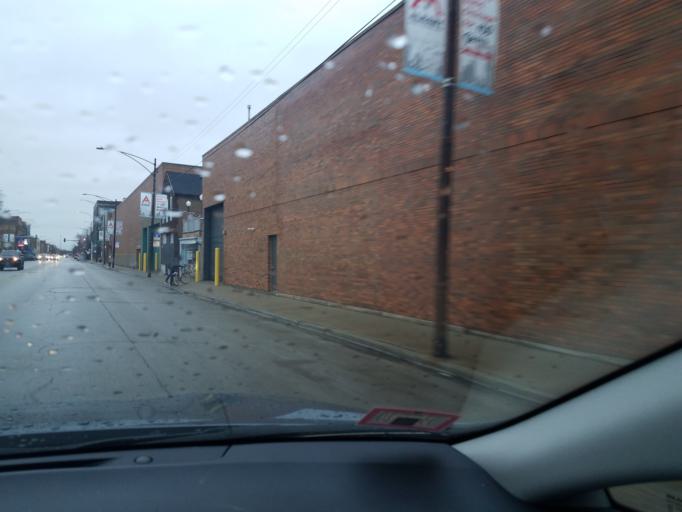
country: US
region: Illinois
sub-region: Cook County
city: Chicago
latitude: 41.8909
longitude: -87.6751
